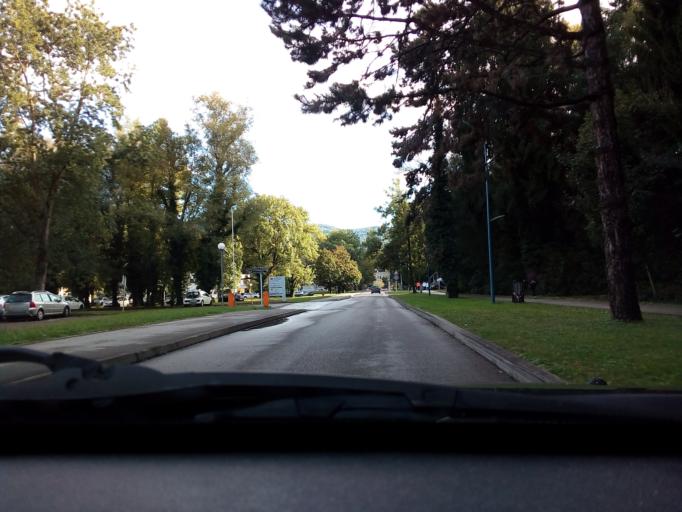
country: FR
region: Rhone-Alpes
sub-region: Departement de l'Isere
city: Corenc
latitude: 45.1975
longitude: 5.7744
